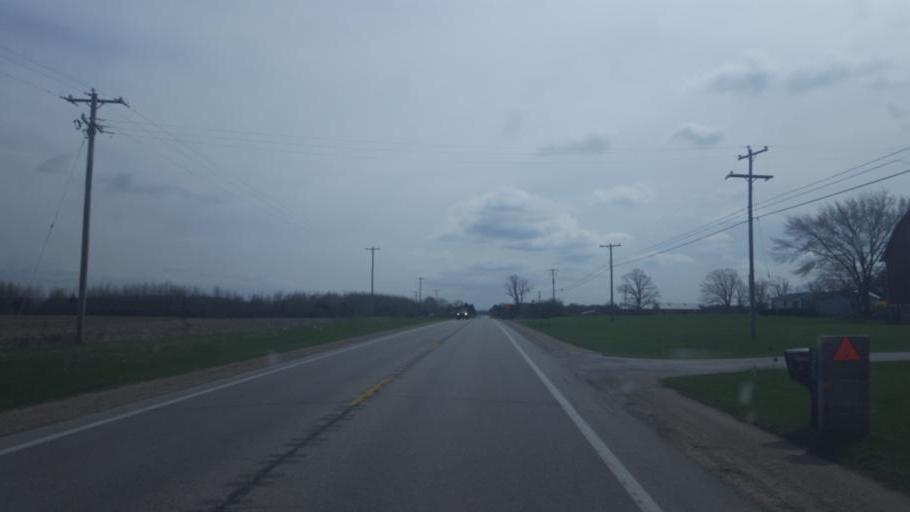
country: US
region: Michigan
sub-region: Montcalm County
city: Edmore
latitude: 43.4080
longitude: -85.0082
